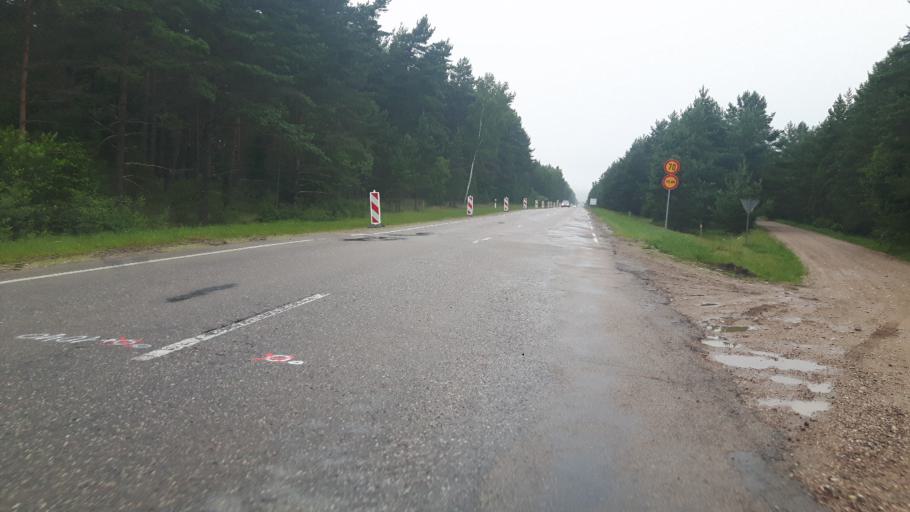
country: LV
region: Rucavas
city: Rucava
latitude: 56.1456
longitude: 21.1507
